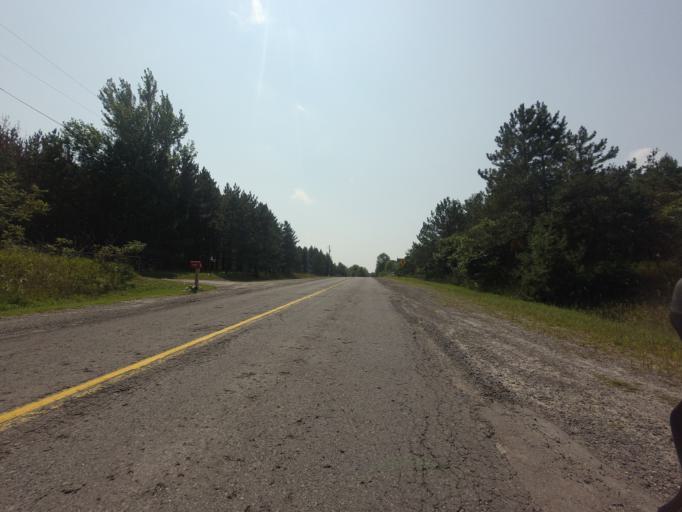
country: CA
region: Ontario
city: Kingston
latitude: 44.6276
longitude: -76.5632
